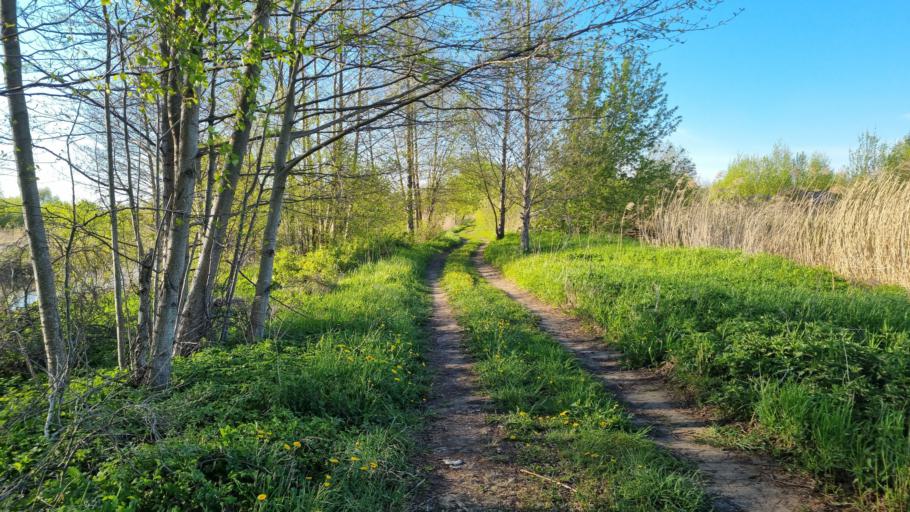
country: LV
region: Riga
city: Bolderaja
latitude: 56.9872
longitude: 24.0587
